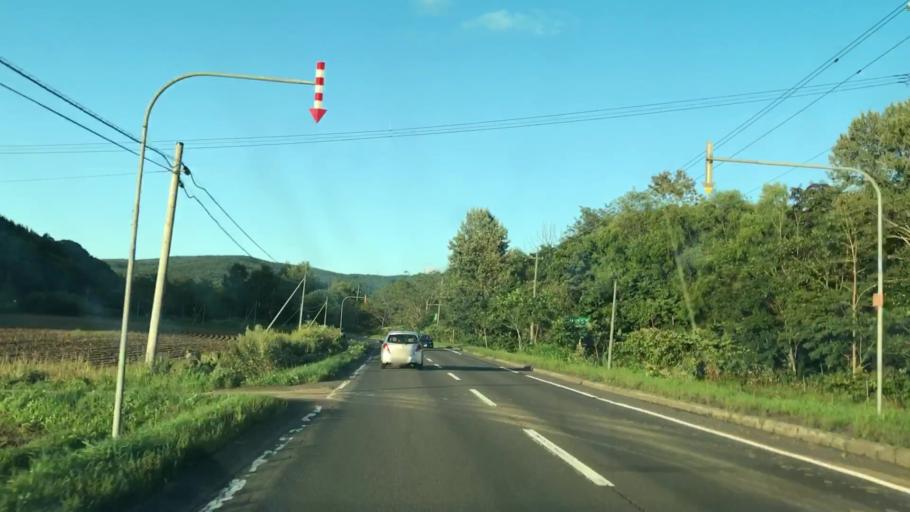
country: JP
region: Hokkaido
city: Niseko Town
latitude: 42.8007
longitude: 140.9891
